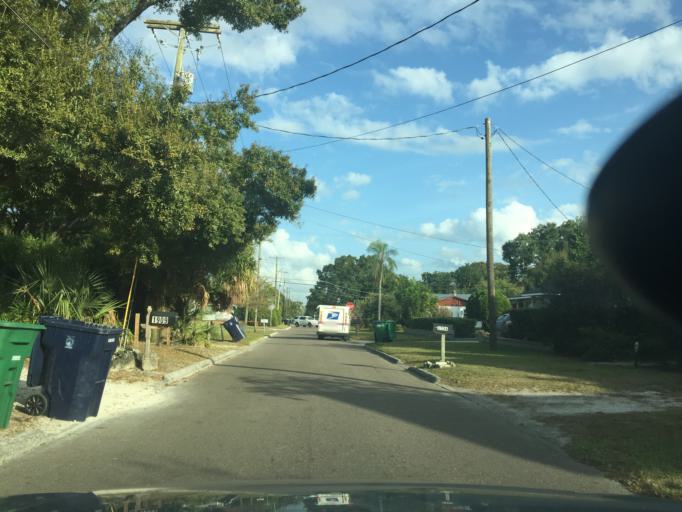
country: US
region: Florida
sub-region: Hillsborough County
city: Tampa
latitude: 27.9535
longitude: -82.4795
